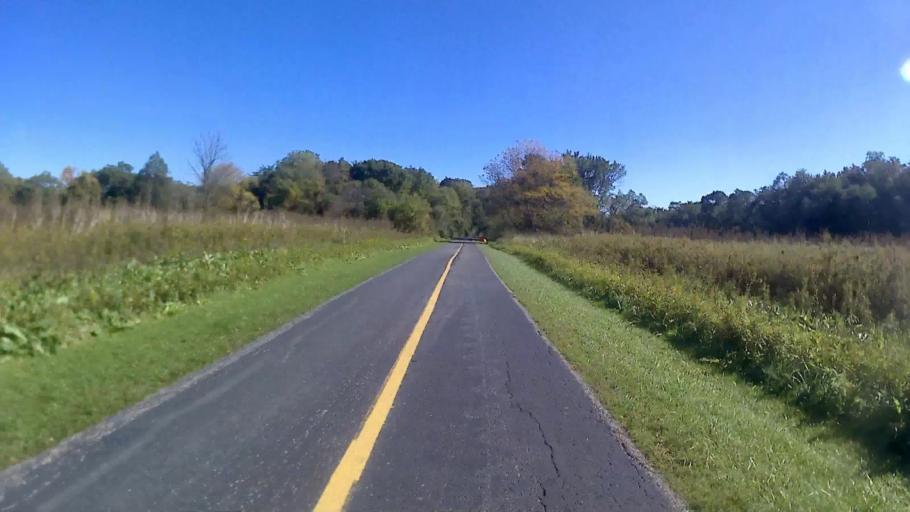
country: US
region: Illinois
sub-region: Cook County
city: Rolling Meadows
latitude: 42.0339
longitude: -88.0175
